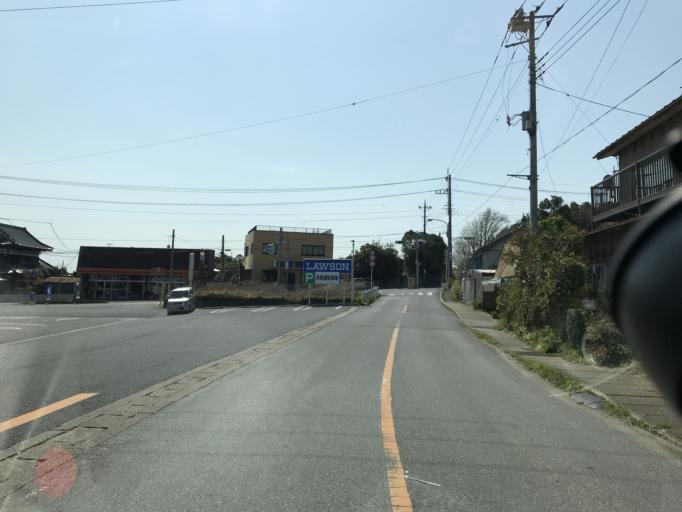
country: JP
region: Chiba
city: Yokaichiba
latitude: 35.7544
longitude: 140.5856
